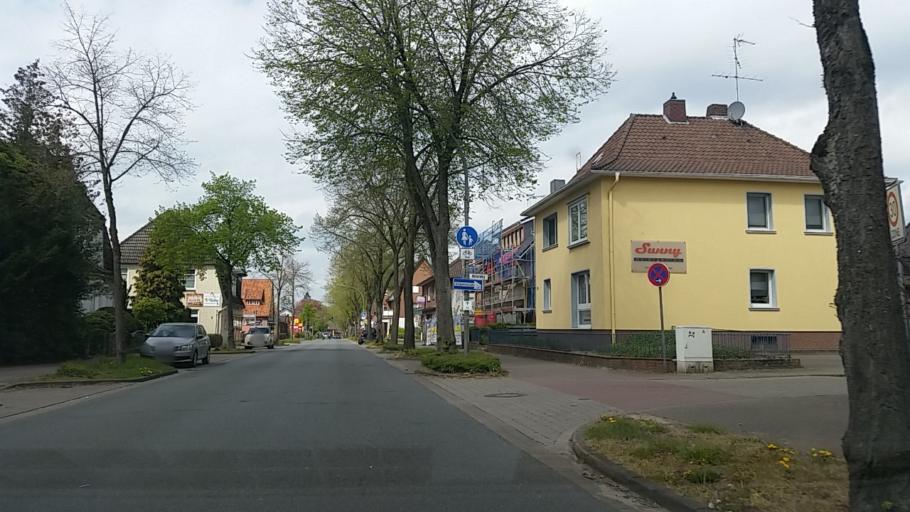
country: DE
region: Lower Saxony
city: Schneverdingen
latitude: 53.1136
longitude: 9.7946
